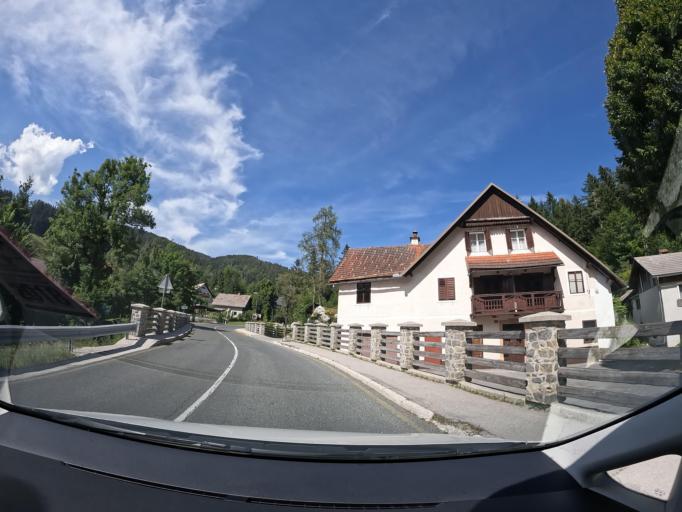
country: AT
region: Carinthia
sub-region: Politischer Bezirk Klagenfurt Land
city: Moosburg
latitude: 46.6593
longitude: 14.1389
